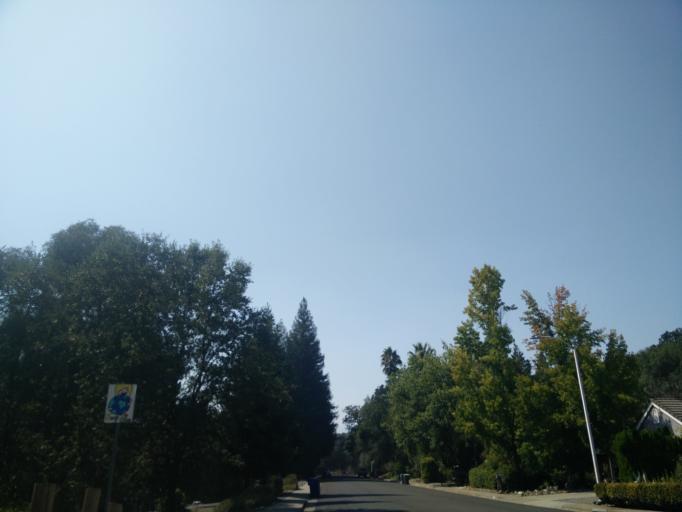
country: US
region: California
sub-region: Shasta County
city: Redding
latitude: 40.5952
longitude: -122.4195
